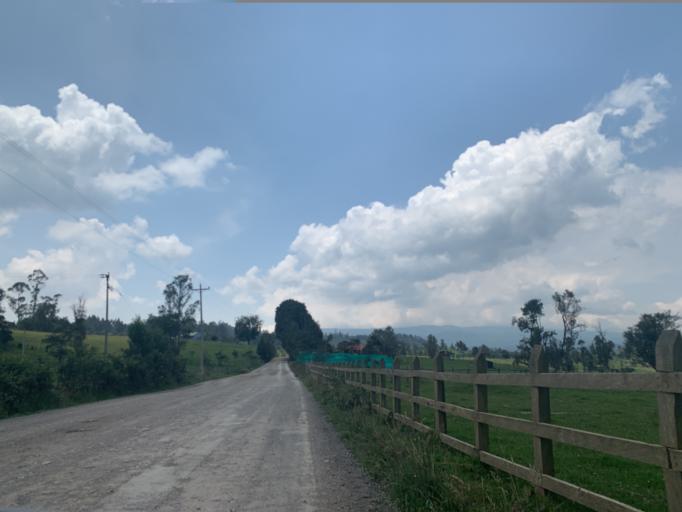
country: CO
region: Boyaca
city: Chiquinquira
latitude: 5.5996
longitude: -73.7633
